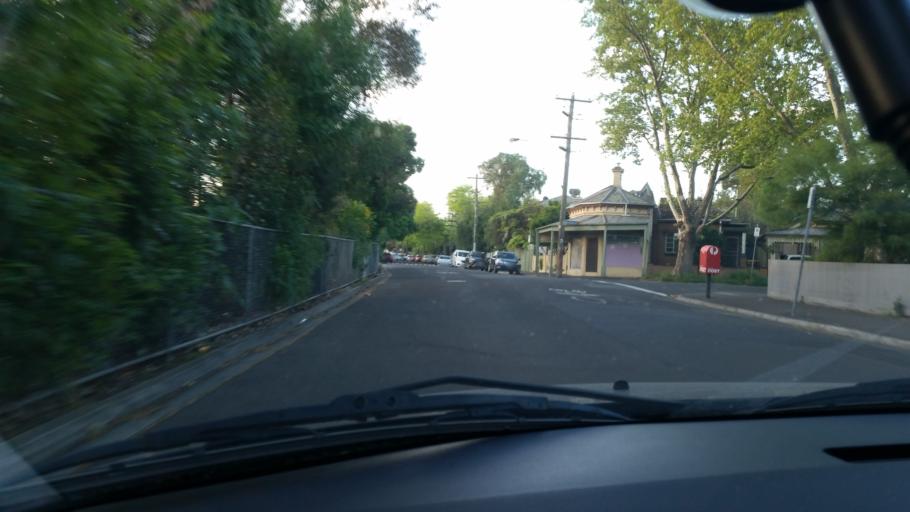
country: AU
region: Victoria
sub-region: Moonee Valley
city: Flemington
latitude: -37.7839
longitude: 144.9283
